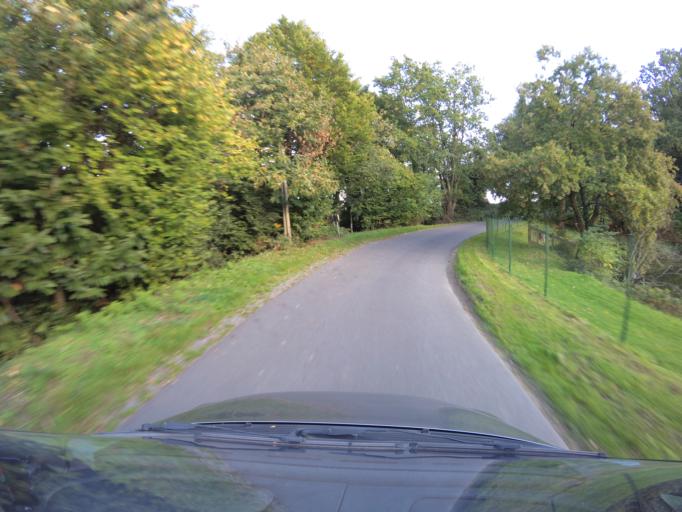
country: FR
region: Brittany
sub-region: Departement du Morbihan
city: Saint-Vincent-sur-Oust
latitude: 47.7165
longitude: -2.1646
